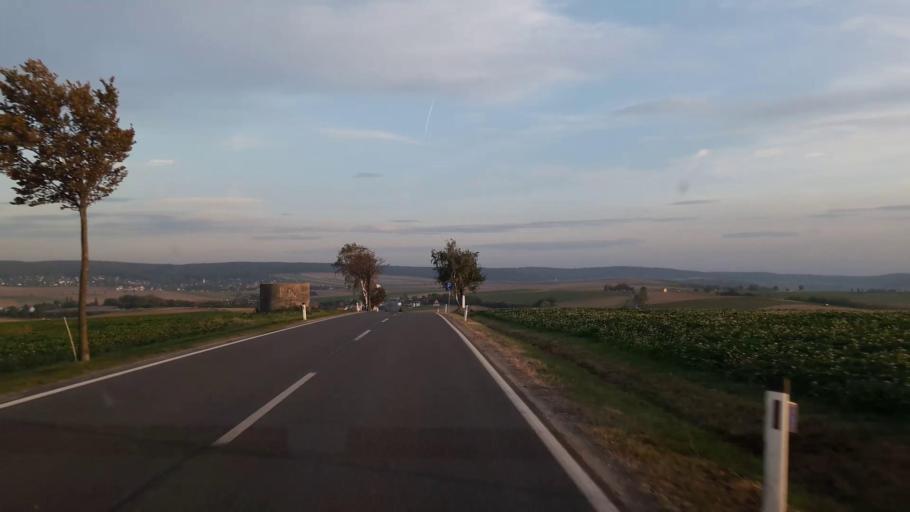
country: AT
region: Lower Austria
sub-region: Politischer Bezirk Korneuburg
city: Grossrussbach
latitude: 48.4487
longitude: 16.3837
